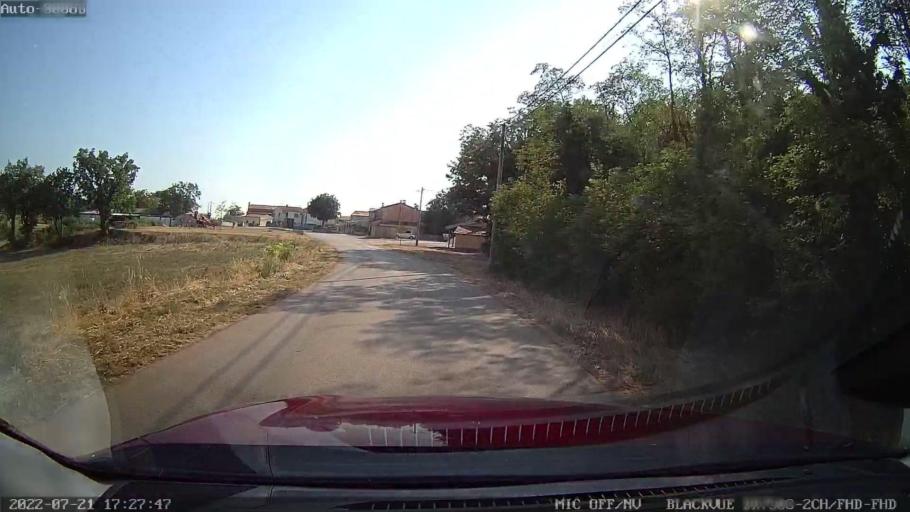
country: HR
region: Istarska
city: Karojba
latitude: 45.1819
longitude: 13.7978
